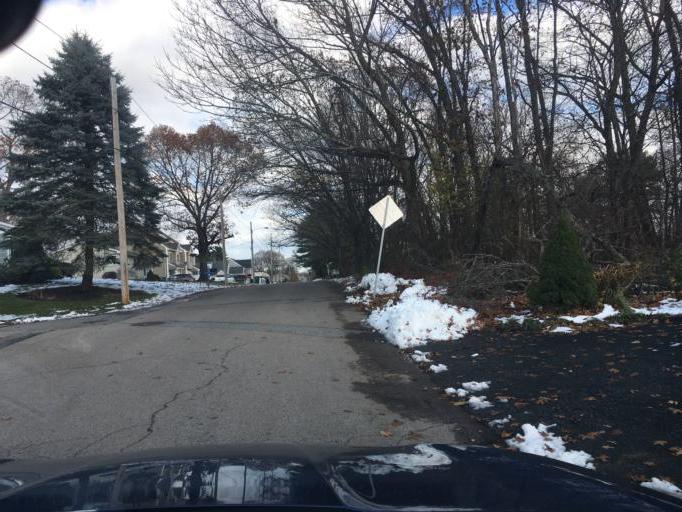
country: US
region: Rhode Island
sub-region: Providence County
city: Pawtucket
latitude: 41.8973
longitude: -71.3677
